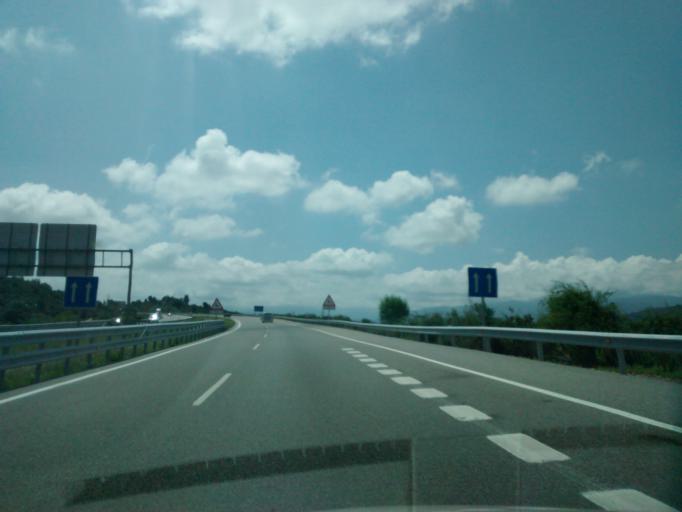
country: ES
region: Castille and Leon
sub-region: Provincia de Leon
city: Ponferrada
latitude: 42.5753
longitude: -6.6021
